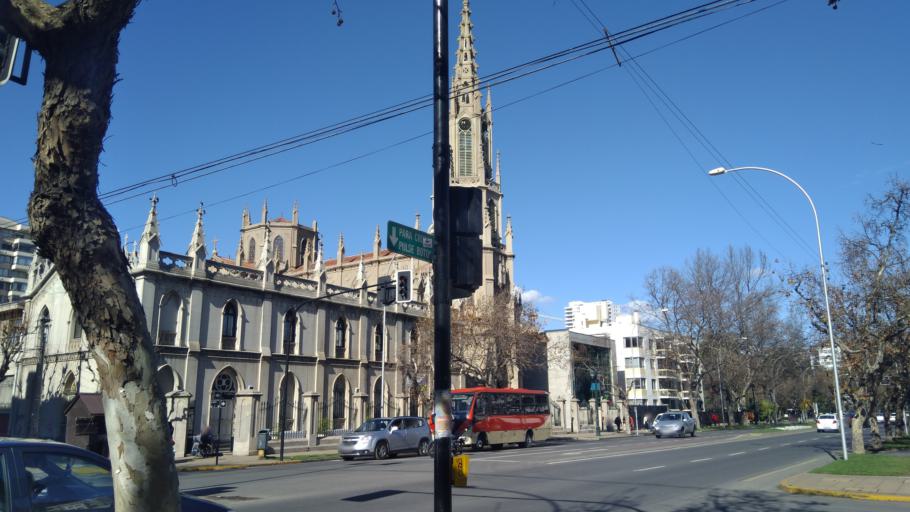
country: CL
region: Valparaiso
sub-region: Provincia de Valparaiso
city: Vina del Mar
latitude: -33.0183
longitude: -71.5508
